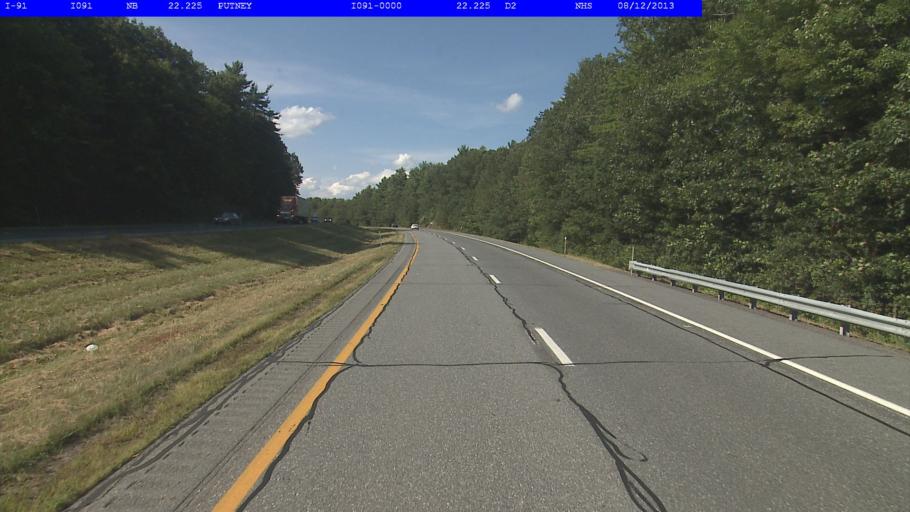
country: US
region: New Hampshire
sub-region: Cheshire County
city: Westmoreland
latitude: 43.0016
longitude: -72.4682
